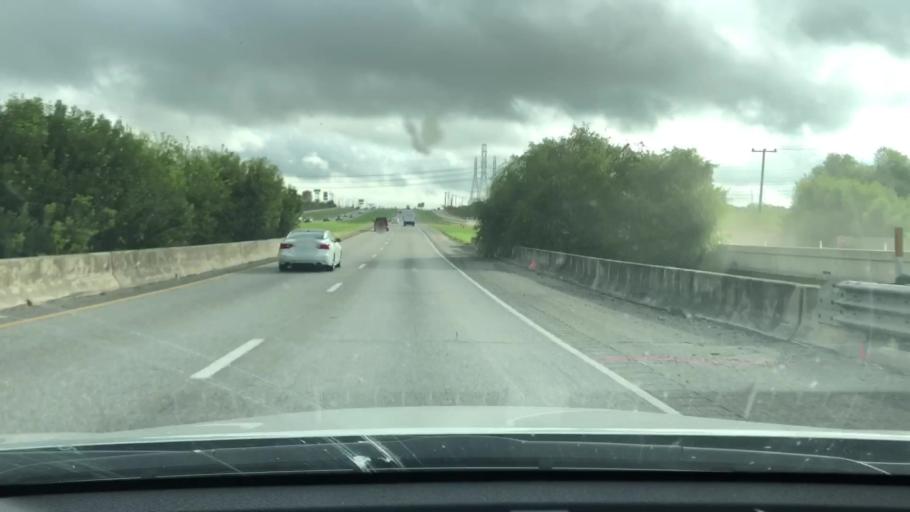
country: US
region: Texas
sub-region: Bexar County
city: Kirby
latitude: 29.4551
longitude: -98.3289
